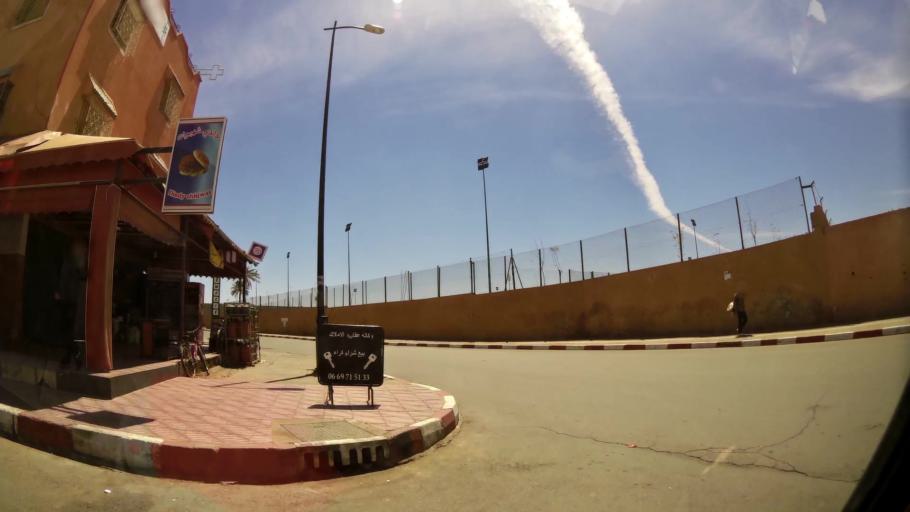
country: MA
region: Marrakech-Tensift-Al Haouz
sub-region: Marrakech
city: Marrakesh
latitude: 31.6563
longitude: -7.9968
